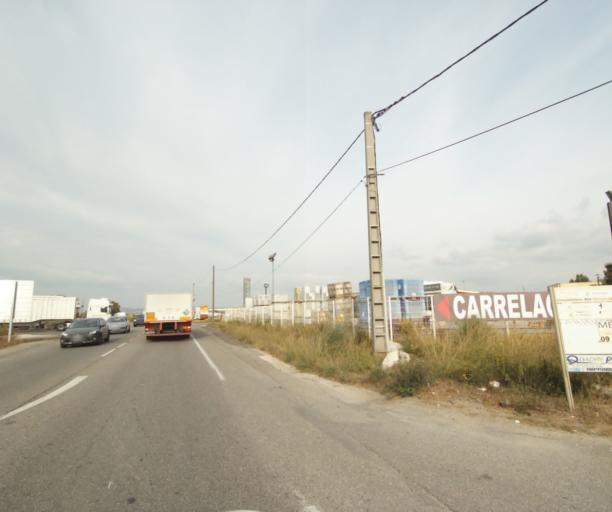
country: FR
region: Provence-Alpes-Cote d'Azur
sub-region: Departement des Bouches-du-Rhone
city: Marignane
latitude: 43.3972
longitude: 5.1983
